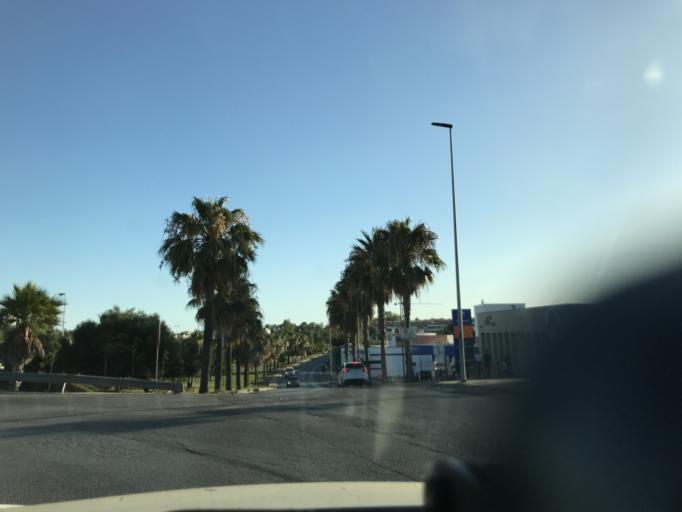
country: ES
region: Andalusia
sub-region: Provincia de Malaga
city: Benahavis
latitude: 36.4621
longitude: -5.0467
